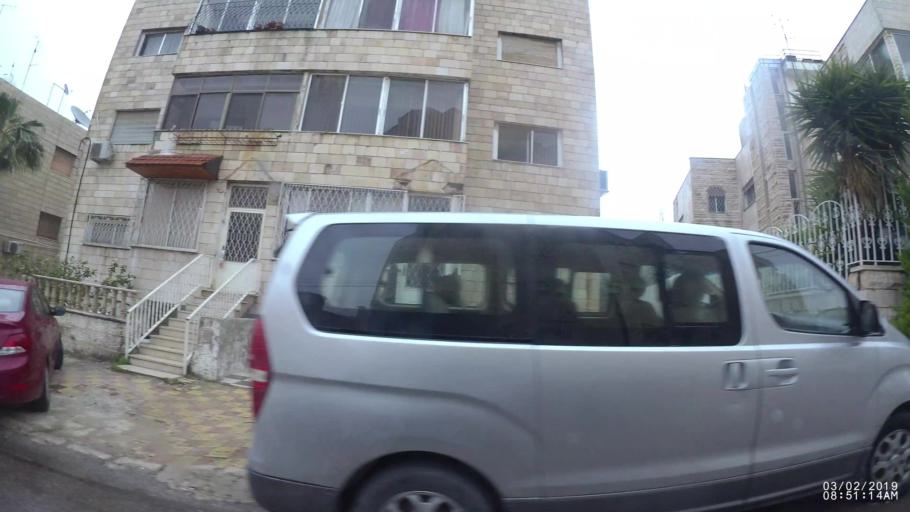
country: JO
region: Amman
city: Wadi as Sir
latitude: 31.9645
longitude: 35.8803
